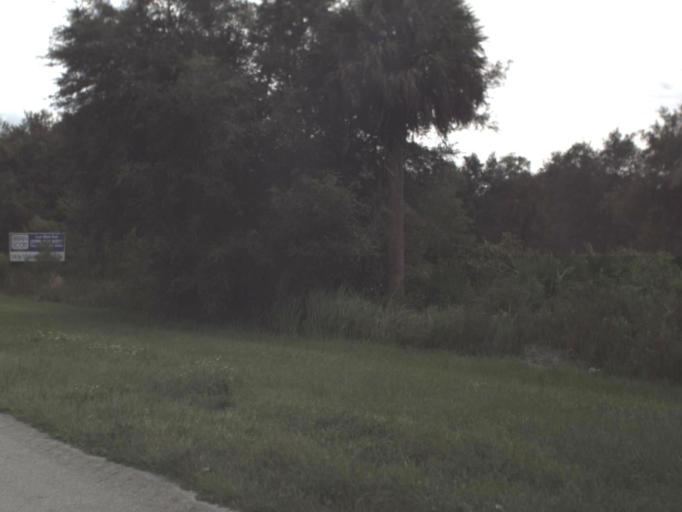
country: US
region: Florida
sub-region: DeSoto County
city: Southeast Arcadia
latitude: 27.1570
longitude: -81.8134
